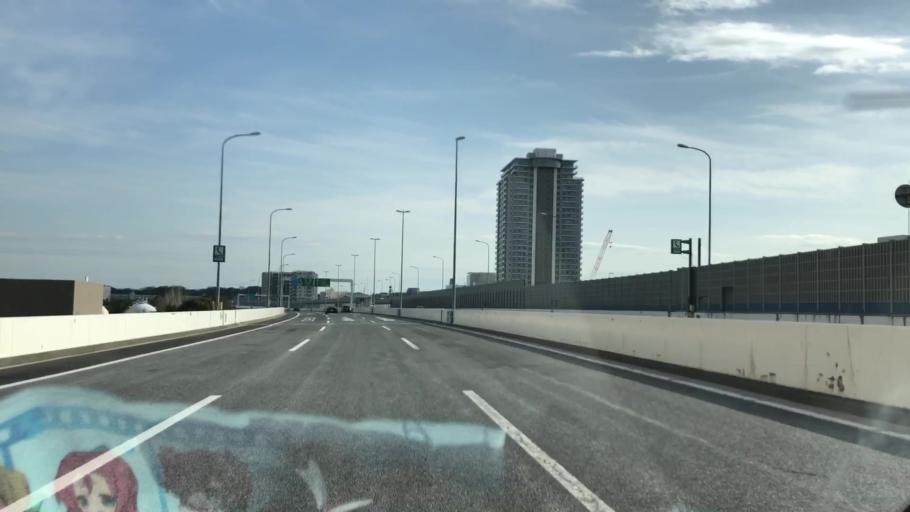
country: JP
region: Kanagawa
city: Yokohama
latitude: 35.3899
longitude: 139.6176
